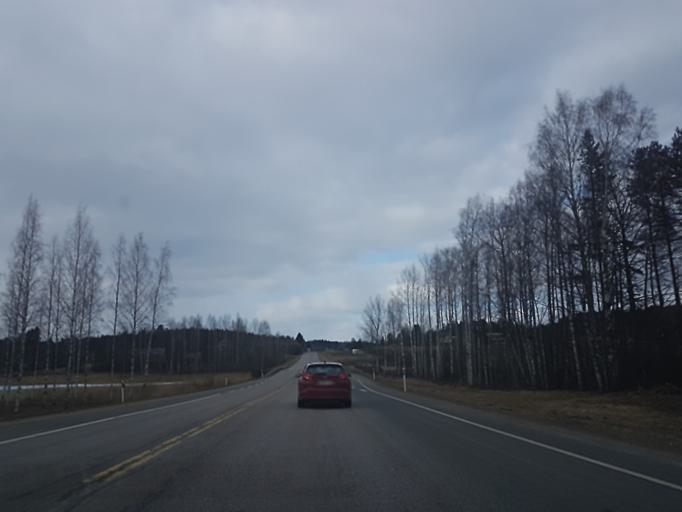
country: FI
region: South Karelia
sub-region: Imatra
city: Parikkala
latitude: 61.4939
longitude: 29.4846
